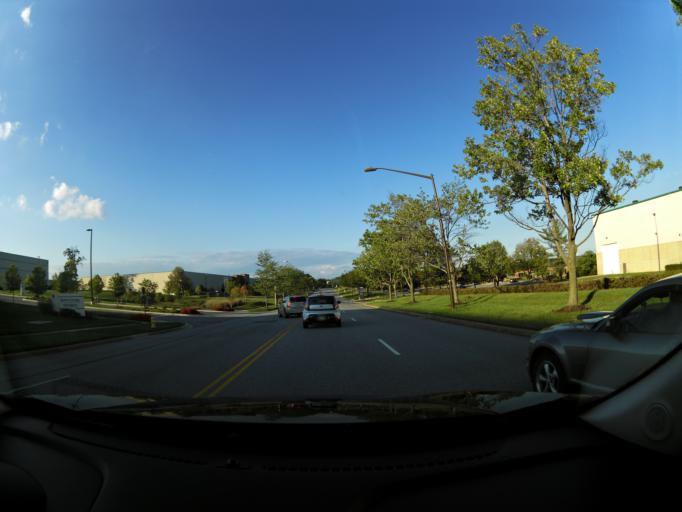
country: US
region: Maryland
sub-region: Howard County
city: Hanover
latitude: 39.1685
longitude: -76.7060
